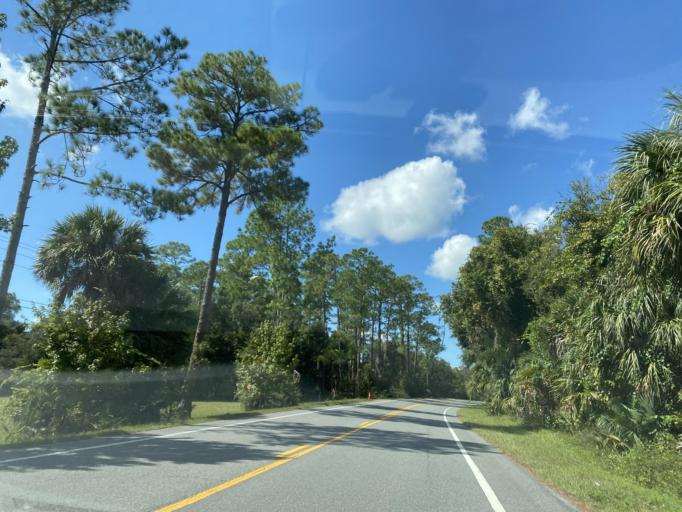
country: US
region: Florida
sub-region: Lake County
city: Lake Mack-Forest Hills
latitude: 29.0095
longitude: -81.4558
